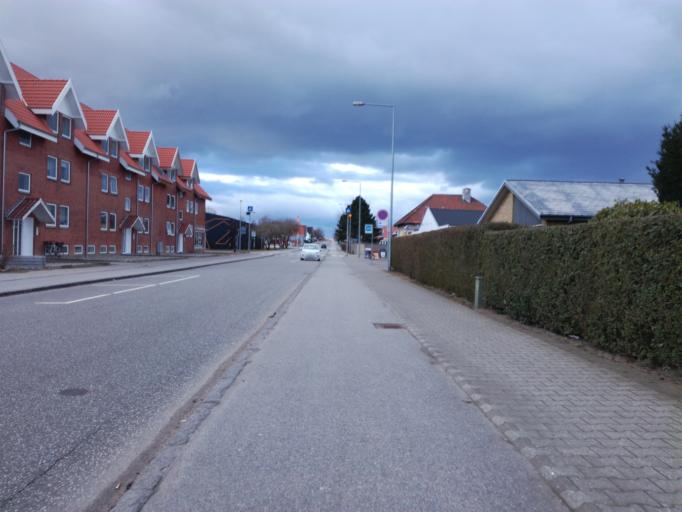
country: DK
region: South Denmark
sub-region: Fredericia Kommune
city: Fredericia
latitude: 55.5767
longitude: 9.7669
